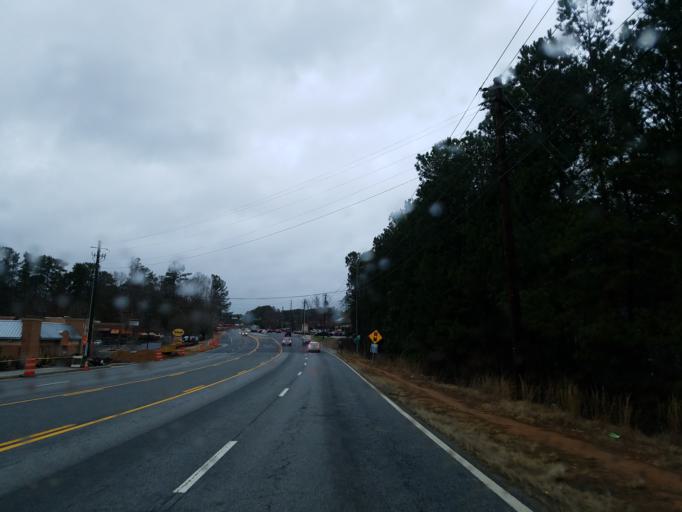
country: US
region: Georgia
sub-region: Gwinnett County
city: Norcross
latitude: 33.9489
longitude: -84.2405
